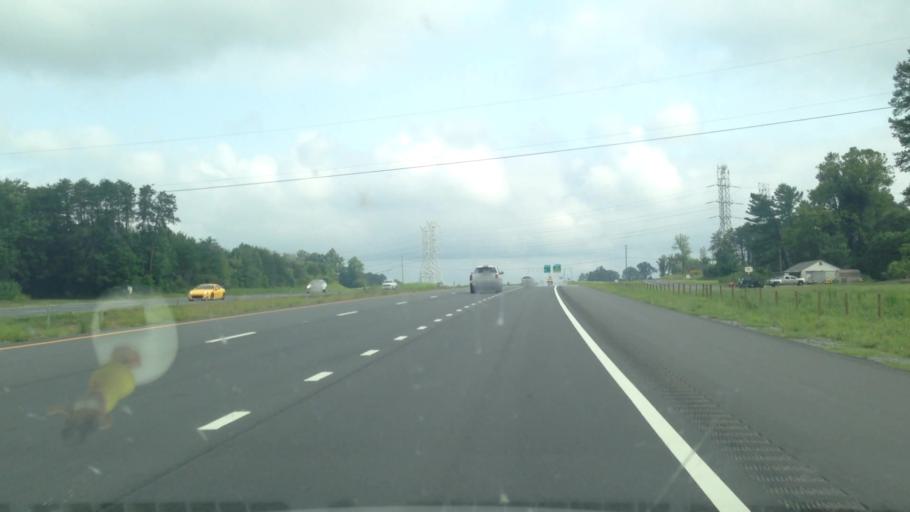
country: US
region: North Carolina
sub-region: Guilford County
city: Summerfield
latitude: 36.2385
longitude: -79.9184
